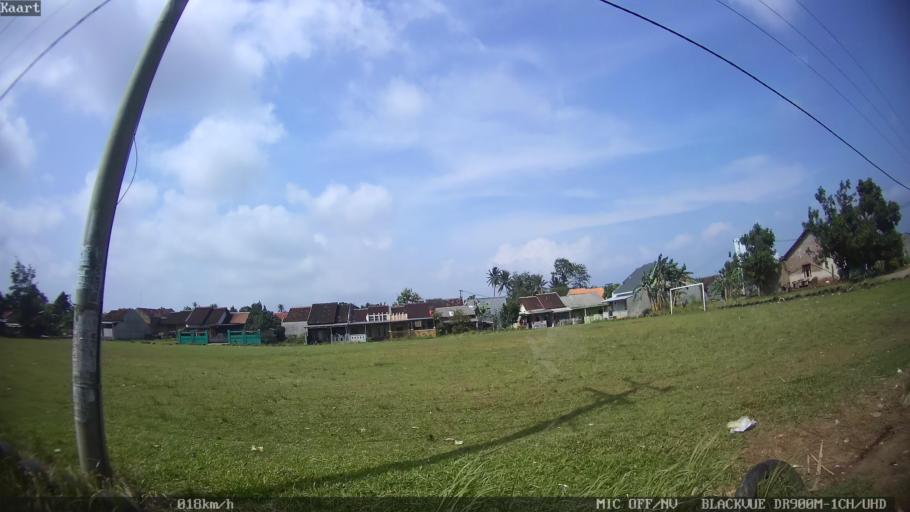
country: ID
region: Lampung
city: Kedaton
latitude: -5.3303
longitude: 105.2808
